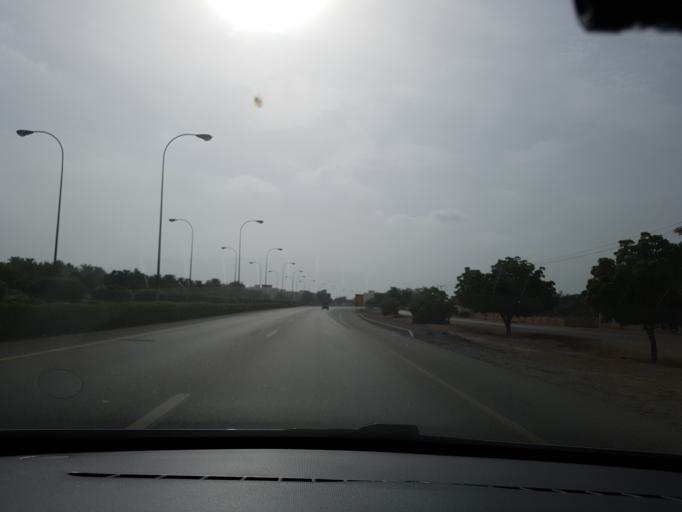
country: OM
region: Al Batinah
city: Al Sohar
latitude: 24.3934
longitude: 56.6895
